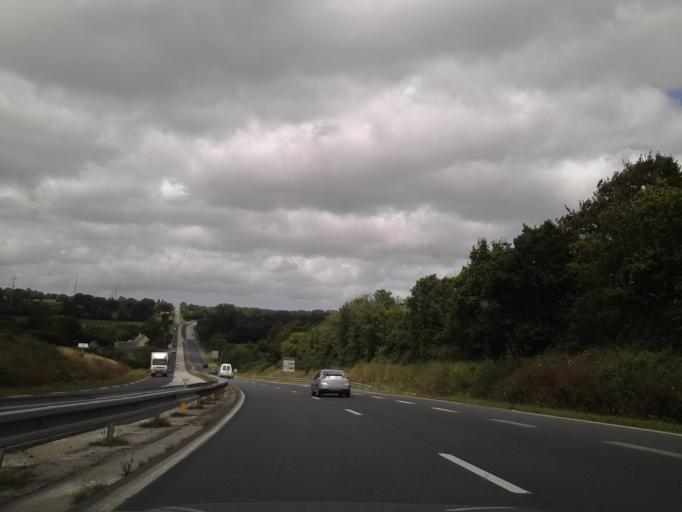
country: FR
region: Lower Normandy
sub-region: Departement de la Manche
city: Brix
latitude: 49.5527
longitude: -1.5613
